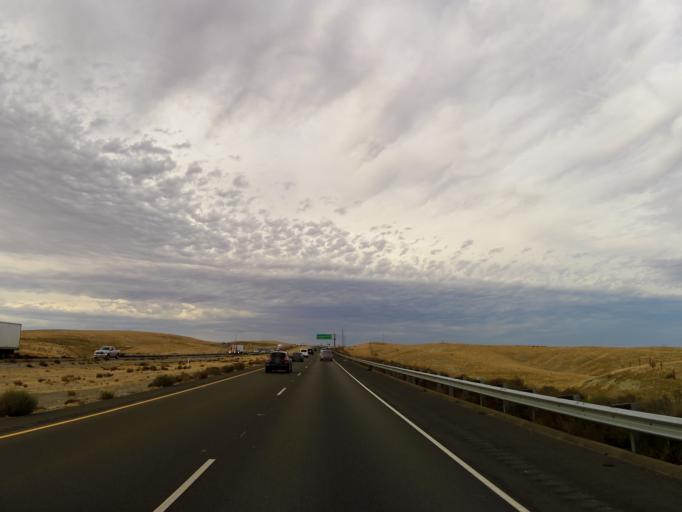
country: US
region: California
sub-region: Kings County
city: Kettleman City
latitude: 35.9764
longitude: -119.9548
